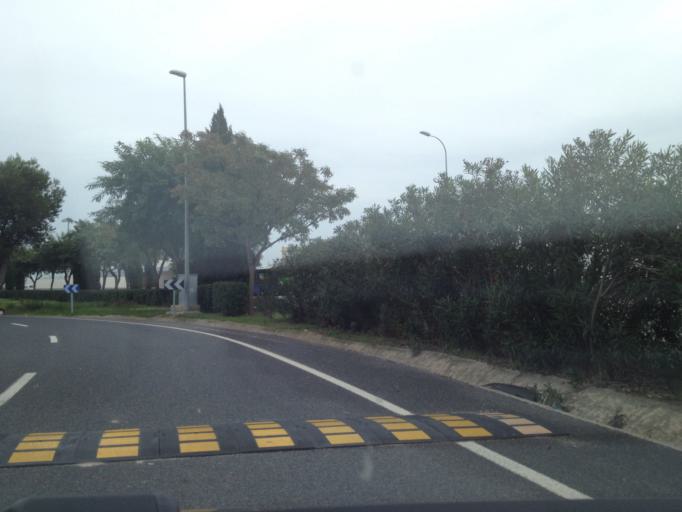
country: ES
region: Balearic Islands
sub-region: Illes Balears
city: s'Arenal
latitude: 39.5442
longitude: 2.7267
